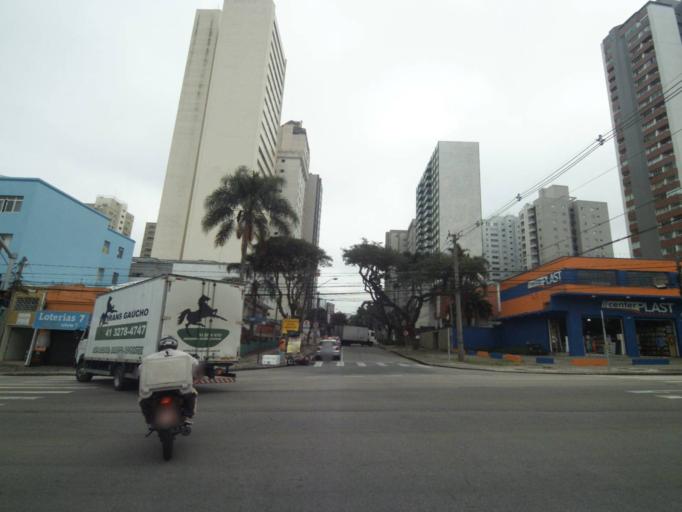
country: BR
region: Parana
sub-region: Curitiba
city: Curitiba
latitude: -25.4339
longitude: -49.2566
